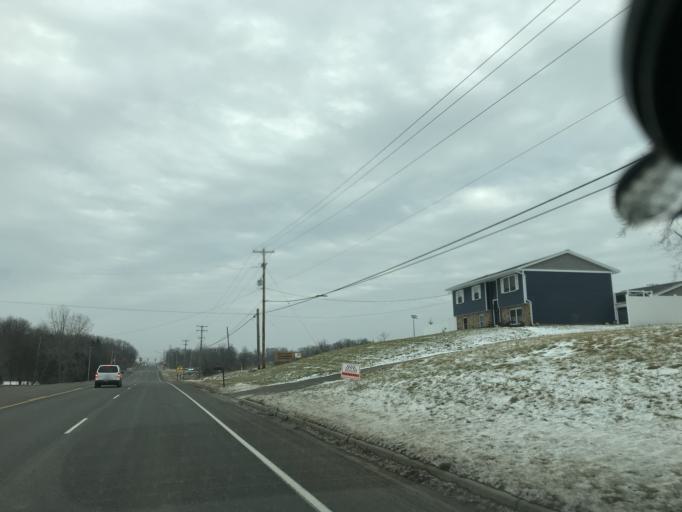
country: US
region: Michigan
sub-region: Kent County
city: Rockford
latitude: 43.1170
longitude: -85.5899
